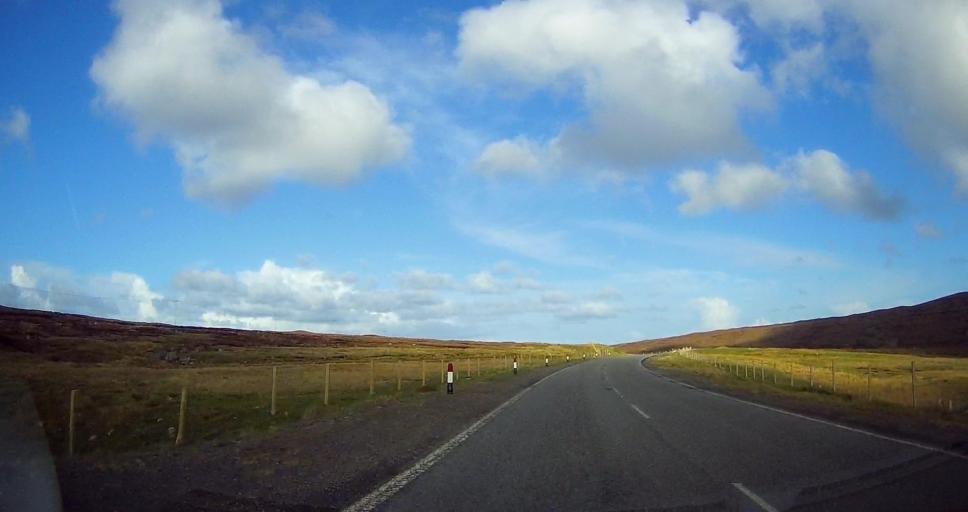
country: GB
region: Scotland
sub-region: Shetland Islands
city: Lerwick
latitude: 60.3495
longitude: -1.2176
